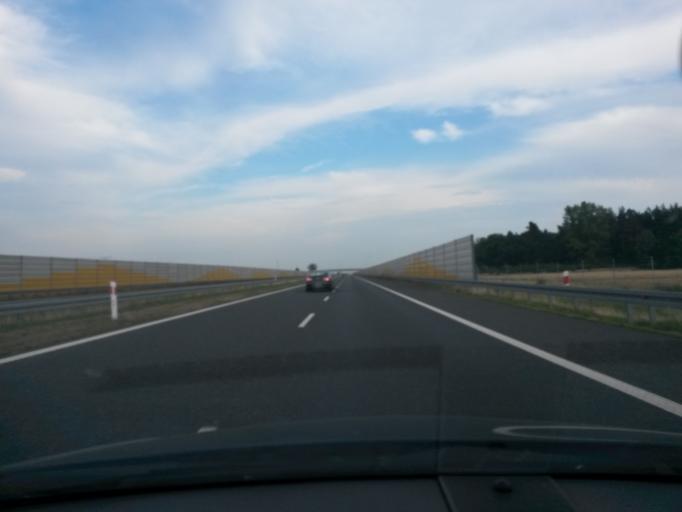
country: PL
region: Lodz Voivodeship
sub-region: Powiat leczycki
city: Swinice Warckie
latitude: 52.0219
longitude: 18.9283
